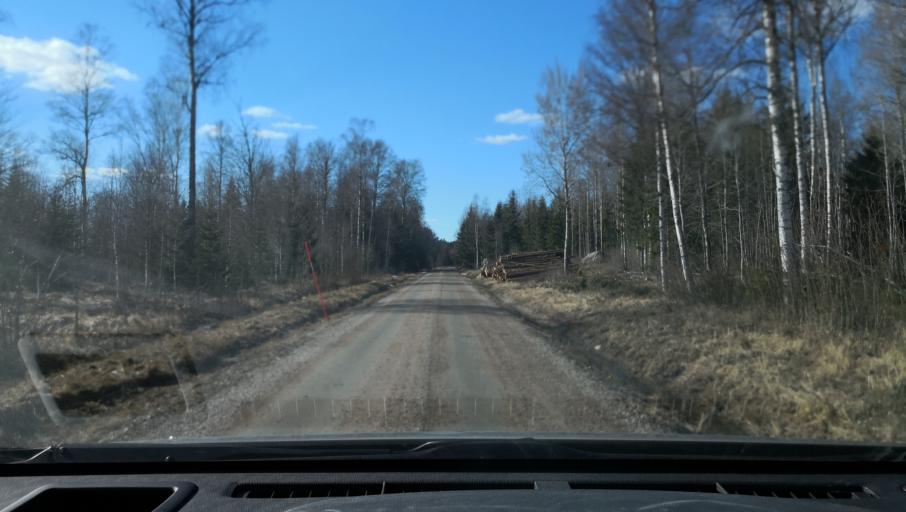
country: SE
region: Vaestmanland
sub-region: Sala Kommun
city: Sala
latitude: 60.1143
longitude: 16.6803
